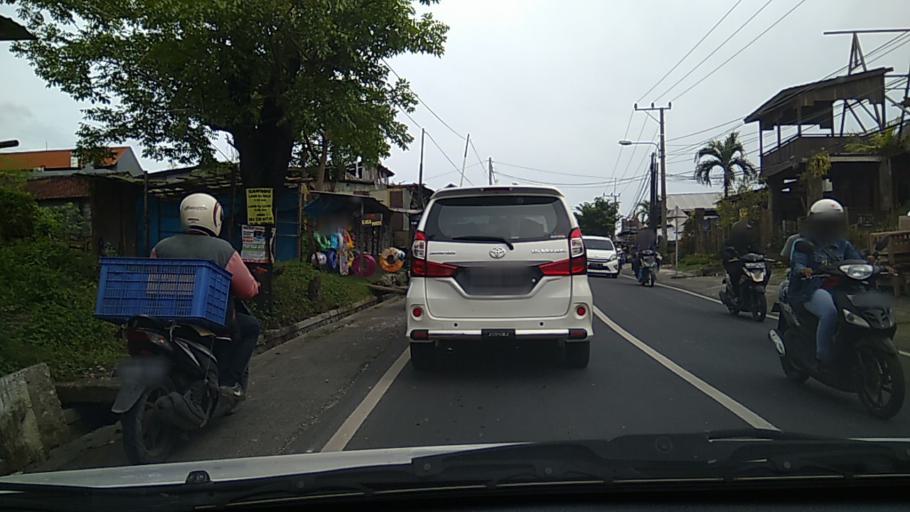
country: ID
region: Bali
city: Banjar Gunungpande
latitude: -8.6390
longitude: 115.1503
